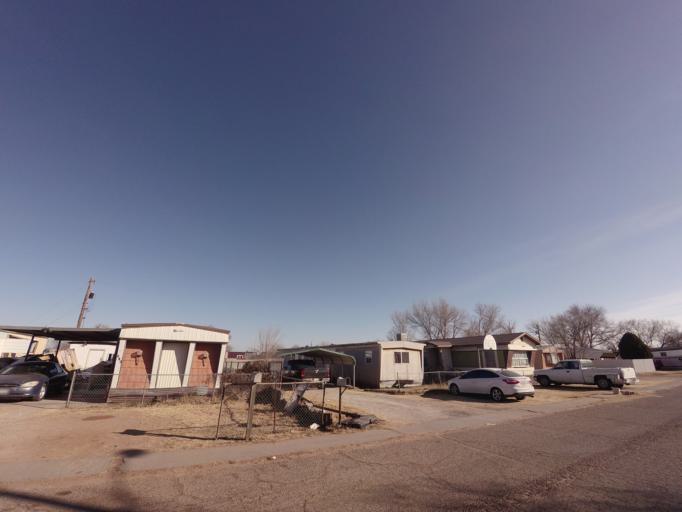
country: US
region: New Mexico
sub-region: Curry County
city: Clovis
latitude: 34.3871
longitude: -103.1984
